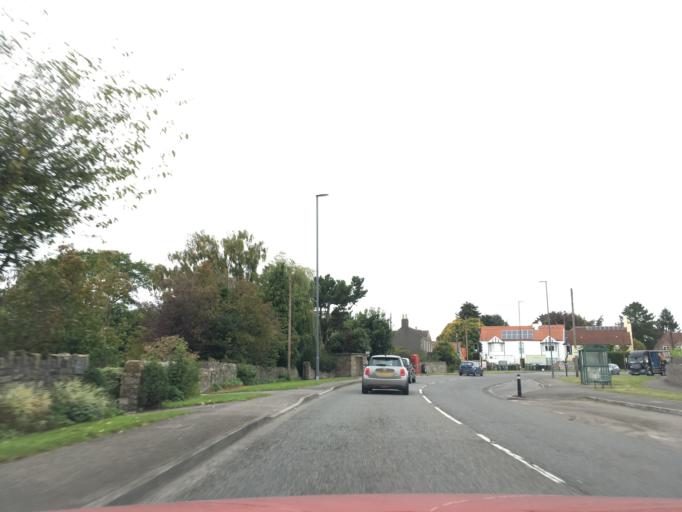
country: GB
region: England
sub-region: South Gloucestershire
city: Alveston
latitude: 51.5916
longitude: -2.5284
